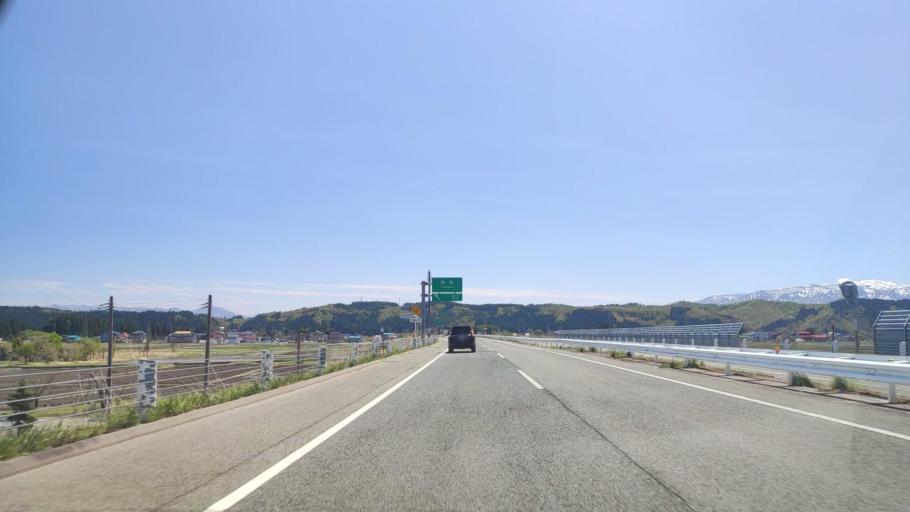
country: JP
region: Yamagata
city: Shinjo
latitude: 38.7076
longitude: 140.3088
